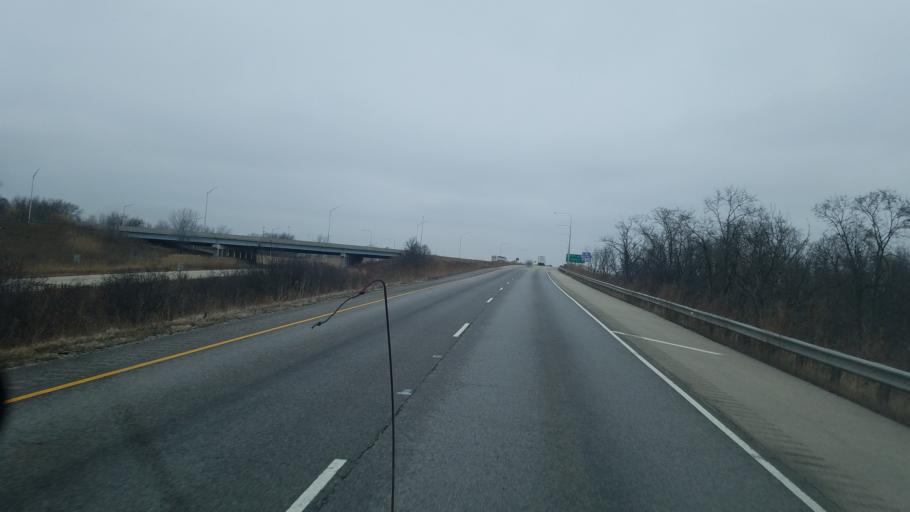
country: US
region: Illinois
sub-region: Lake County
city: Wadsworth
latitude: 42.4773
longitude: -87.9471
